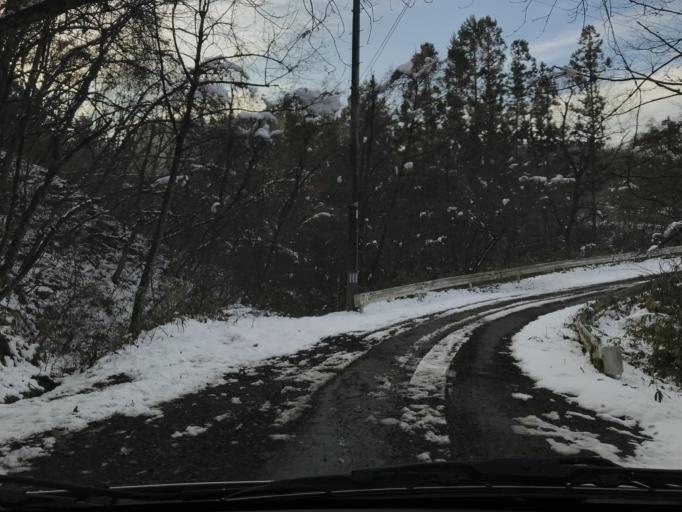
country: JP
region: Iwate
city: Mizusawa
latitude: 39.0405
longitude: 141.1020
